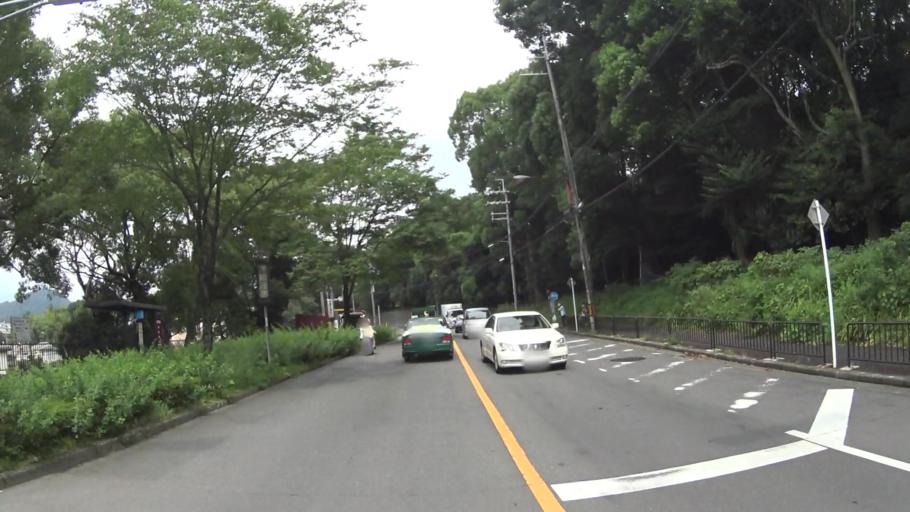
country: JP
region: Kyoto
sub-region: Kyoto-shi
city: Kamigyo-ku
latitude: 35.0646
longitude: 135.7503
